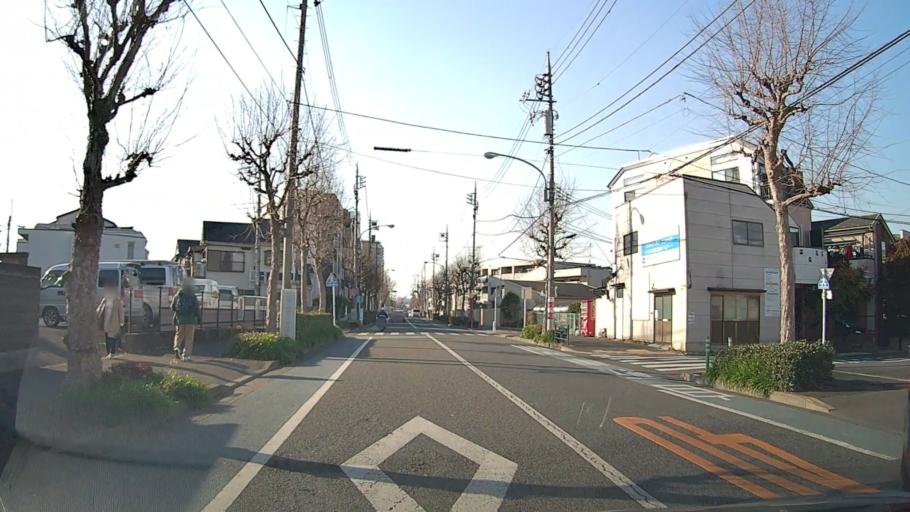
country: JP
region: Saitama
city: Wako
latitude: 35.7495
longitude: 139.6460
